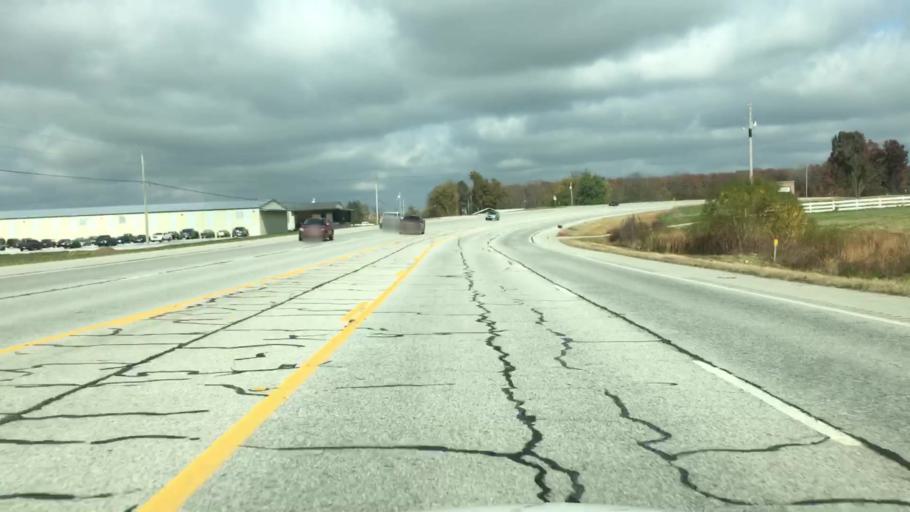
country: US
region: Arkansas
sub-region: Benton County
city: Gentry
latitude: 36.2290
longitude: -94.4951
